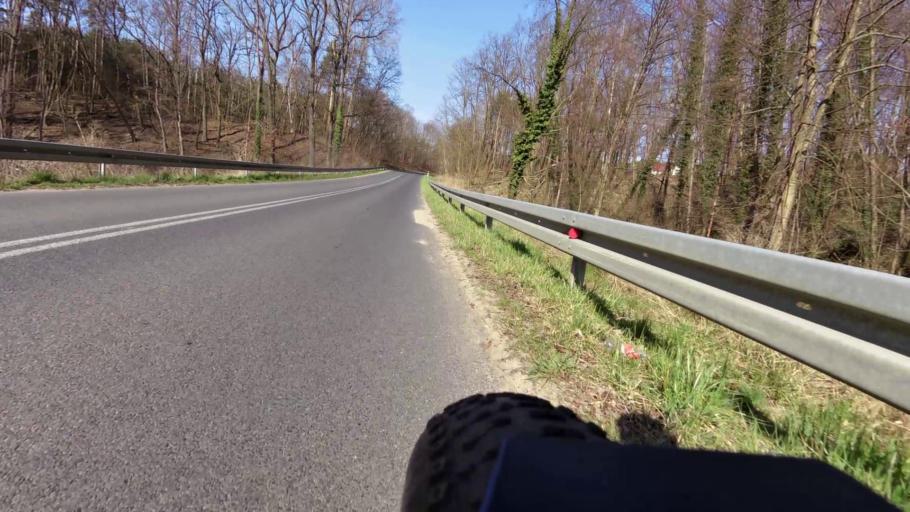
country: PL
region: Lubusz
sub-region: Powiat slubicki
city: Cybinka
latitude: 52.2256
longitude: 14.8397
